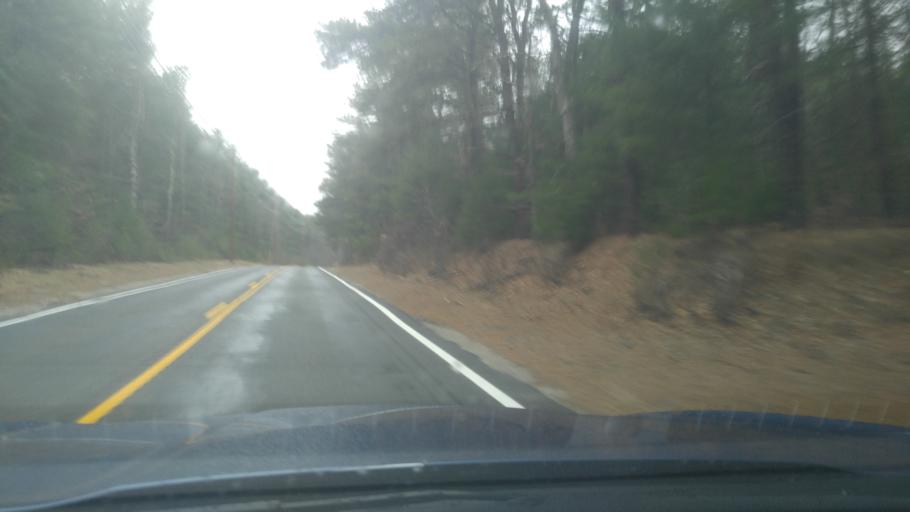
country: US
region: Rhode Island
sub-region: Kent County
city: West Greenwich
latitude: 41.6473
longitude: -71.5827
